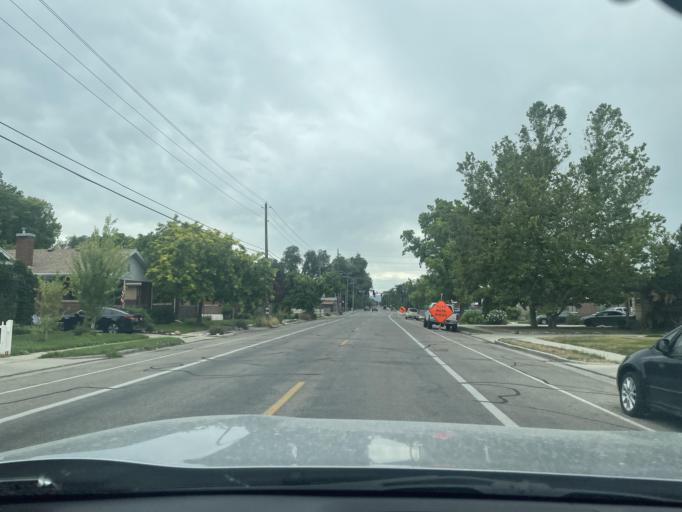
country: US
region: Utah
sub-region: Salt Lake County
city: South Salt Lake
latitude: 40.7143
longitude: -111.8769
